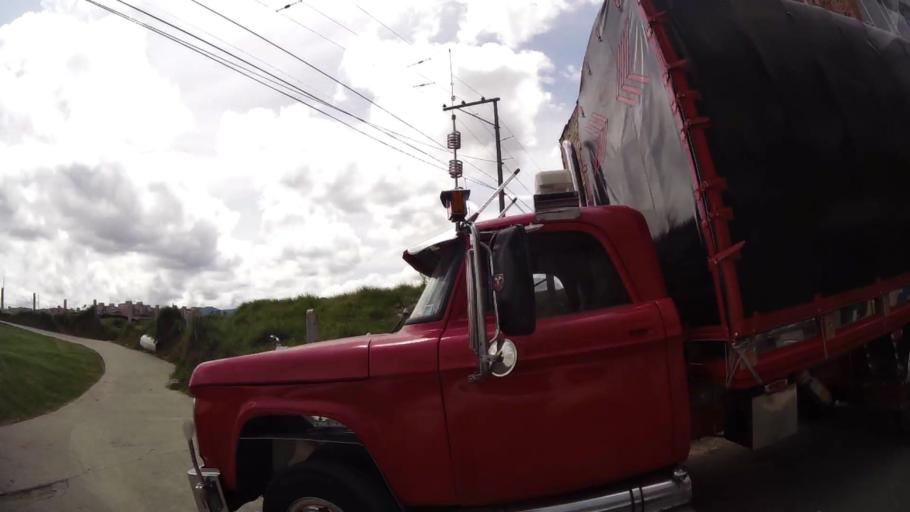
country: CO
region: Bogota D.C.
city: Bogota
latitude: 4.6552
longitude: -74.1356
